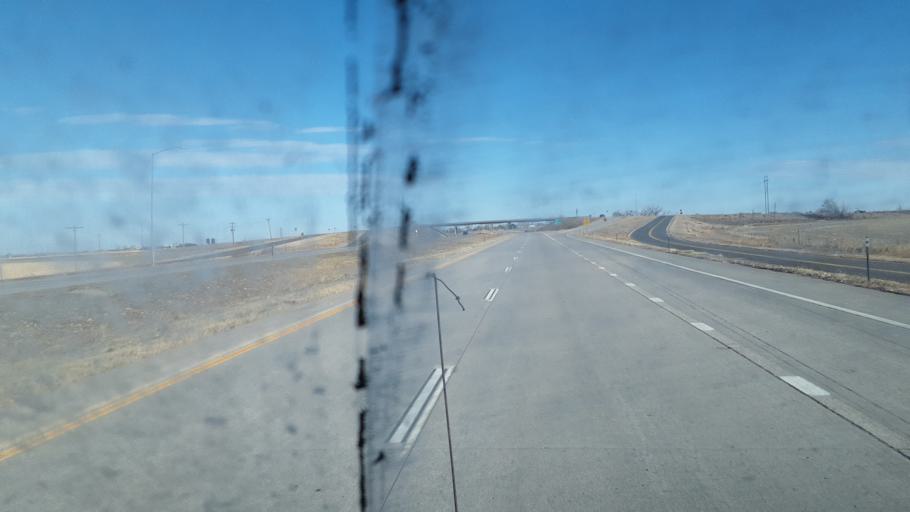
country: US
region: Colorado
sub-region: Morgan County
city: Fort Morgan
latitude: 40.2323
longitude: -104.0987
